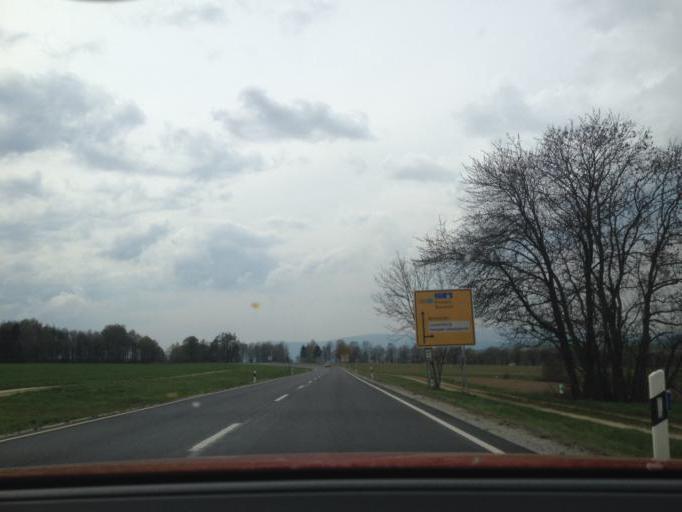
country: DE
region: Bavaria
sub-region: Upper Franconia
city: Bad Alexandersbad
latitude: 50.0227
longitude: 12.0045
